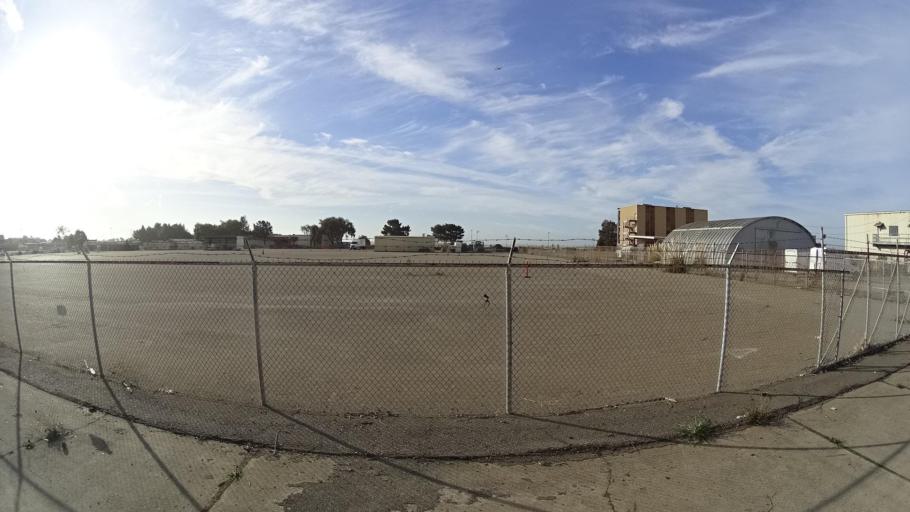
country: US
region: California
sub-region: Alameda County
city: Oakland
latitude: 37.7740
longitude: -122.2951
